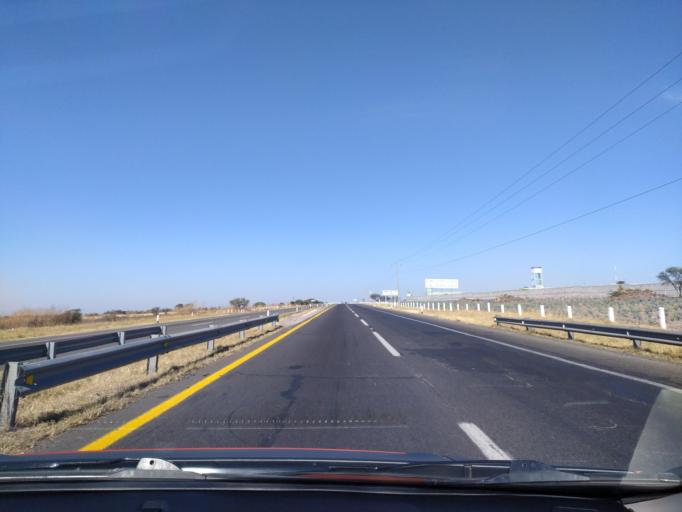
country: MX
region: Jalisco
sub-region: San Juan de los Lagos
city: Mezquitic de la Magdalena
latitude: 21.2896
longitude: -102.1976
